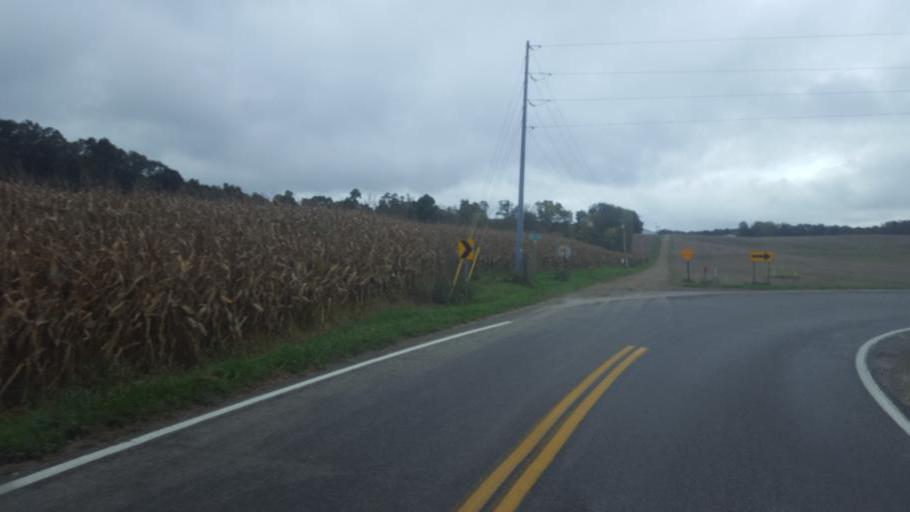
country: US
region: Ohio
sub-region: Ashland County
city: Loudonville
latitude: 40.6342
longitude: -82.2688
